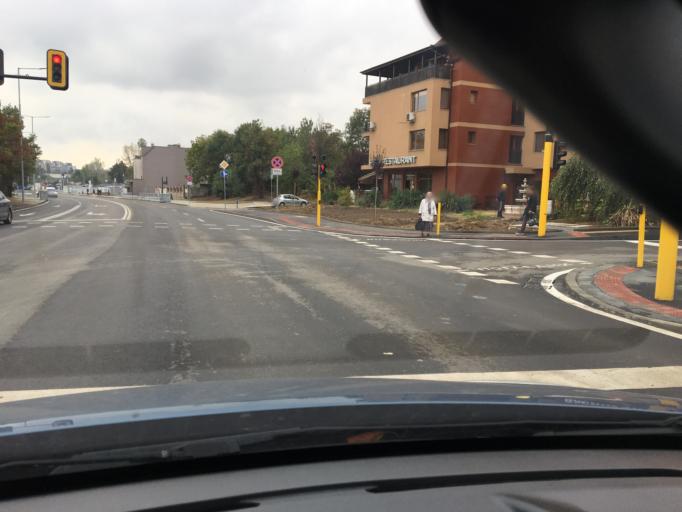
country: BG
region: Sofia-Capital
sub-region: Stolichna Obshtina
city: Sofia
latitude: 42.6844
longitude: 23.2685
